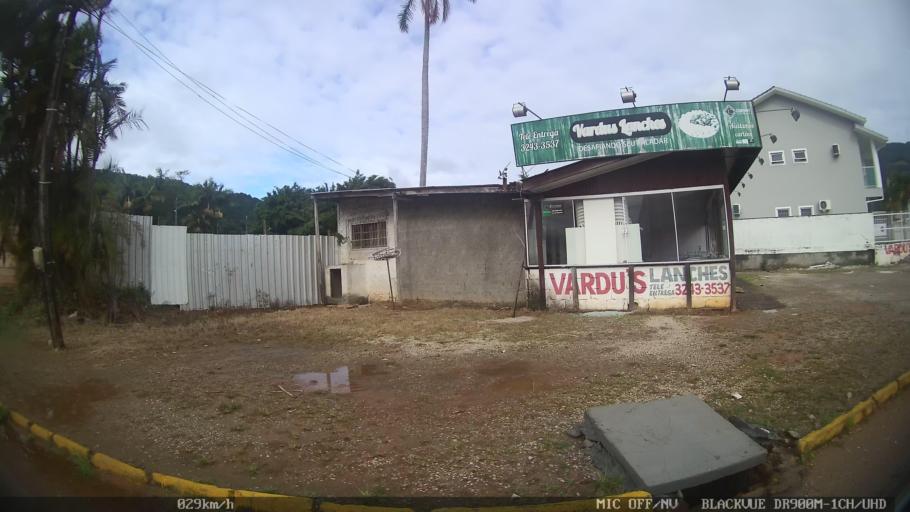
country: BR
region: Santa Catarina
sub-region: Biguacu
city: Biguacu
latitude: -27.5173
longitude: -48.6508
